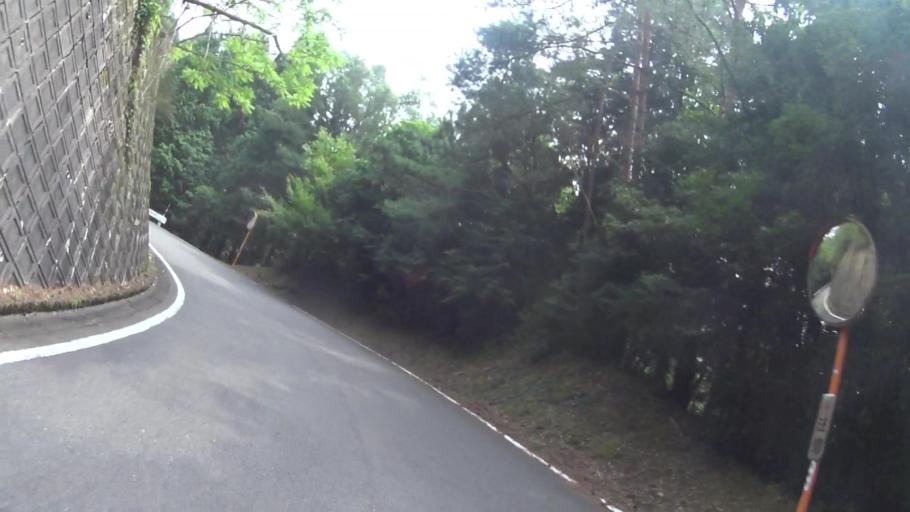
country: JP
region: Kyoto
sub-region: Kyoto-shi
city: Kamigyo-ku
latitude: 35.2074
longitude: 135.6675
